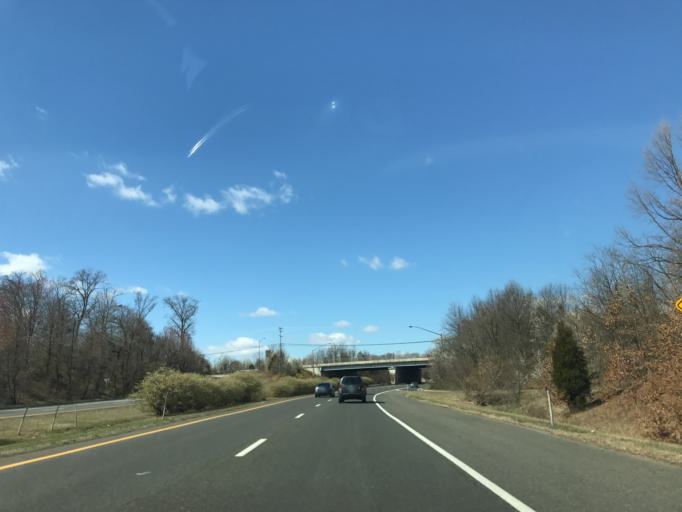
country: US
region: Maryland
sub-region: Anne Arundel County
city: Parole
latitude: 38.9715
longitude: -76.5398
